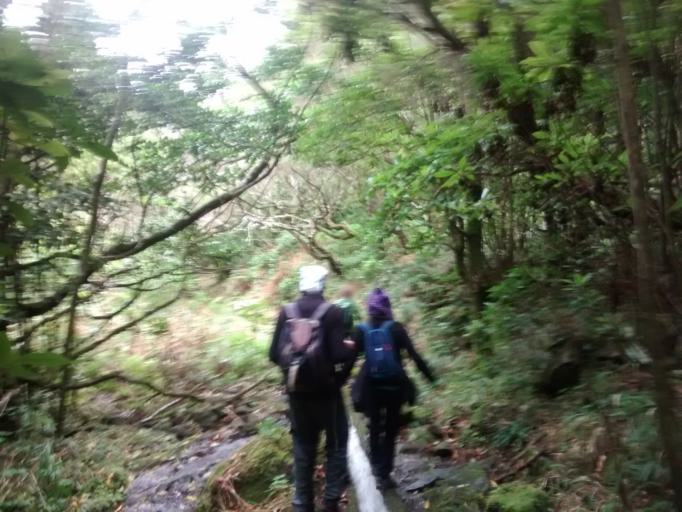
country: PT
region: Madeira
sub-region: Sao Vicente
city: Sao Vicente
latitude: 32.7569
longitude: -17.0477
